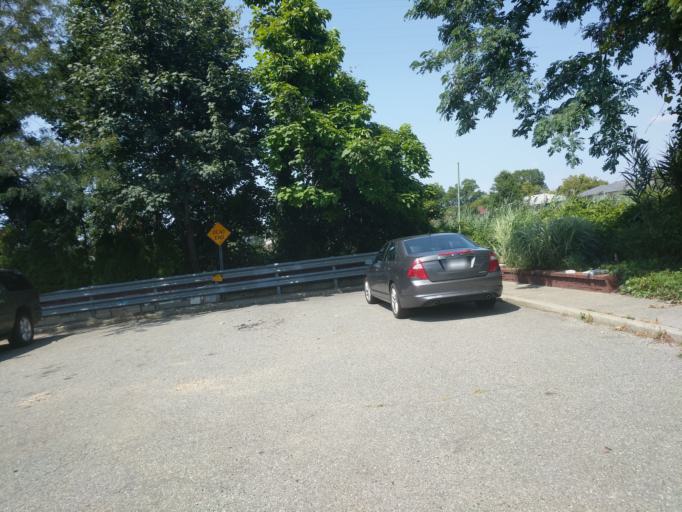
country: US
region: New York
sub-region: Nassau County
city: Woodmere
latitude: 40.6405
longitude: -73.7275
